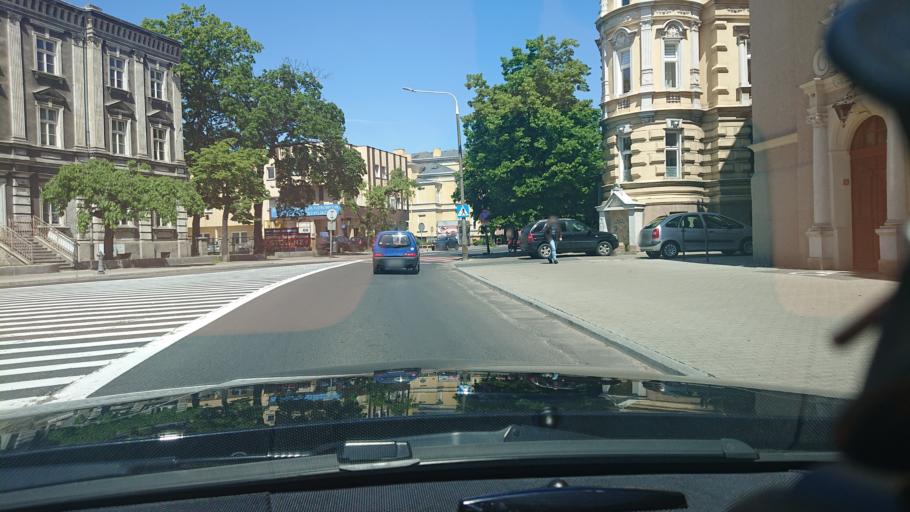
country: PL
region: Greater Poland Voivodeship
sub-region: Powiat gnieznienski
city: Gniezno
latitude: 52.5310
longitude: 17.6022
